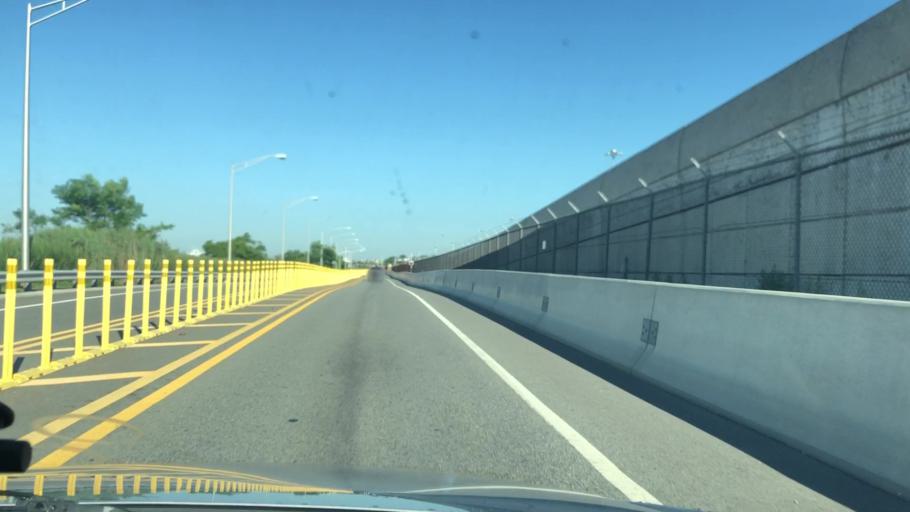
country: US
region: New York
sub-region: Queens County
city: Borough of Queens
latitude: 40.6614
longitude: -73.8142
